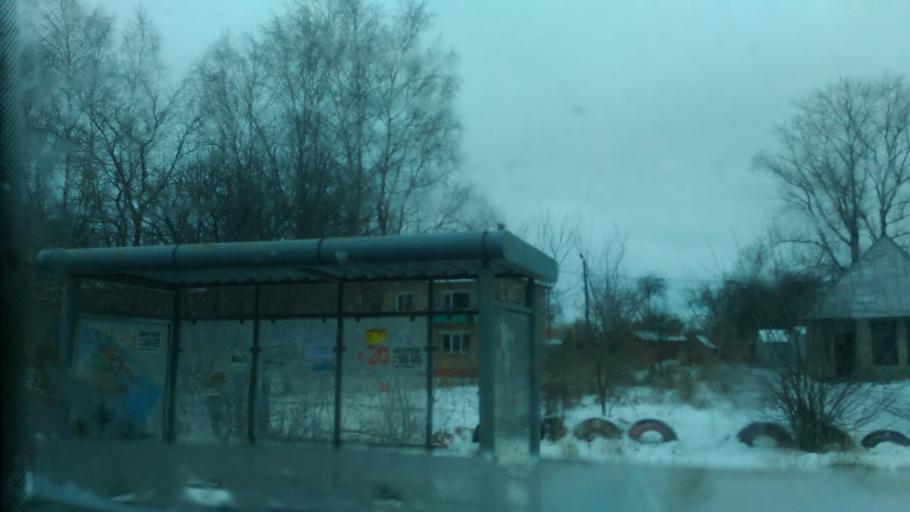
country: RU
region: Tula
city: Bolokhovo
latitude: 54.0658
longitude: 37.7989
